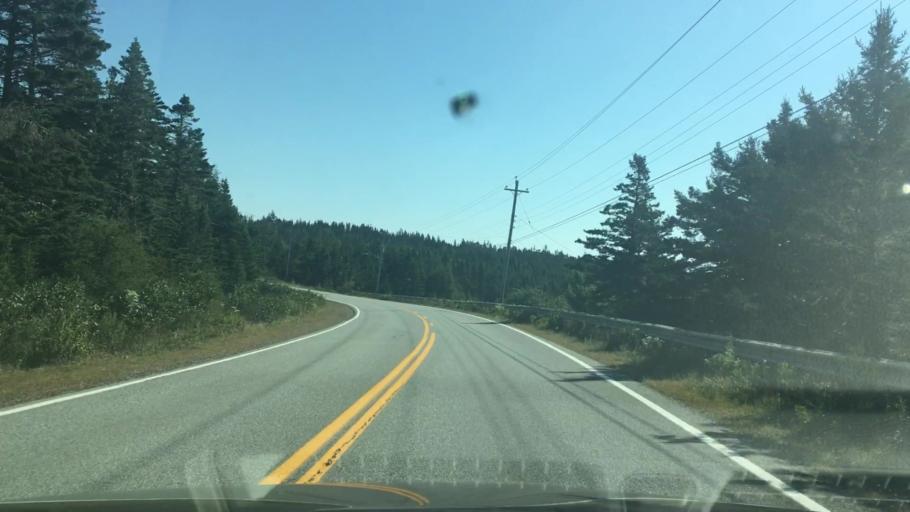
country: CA
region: Nova Scotia
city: Cole Harbour
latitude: 44.7775
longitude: -62.7864
